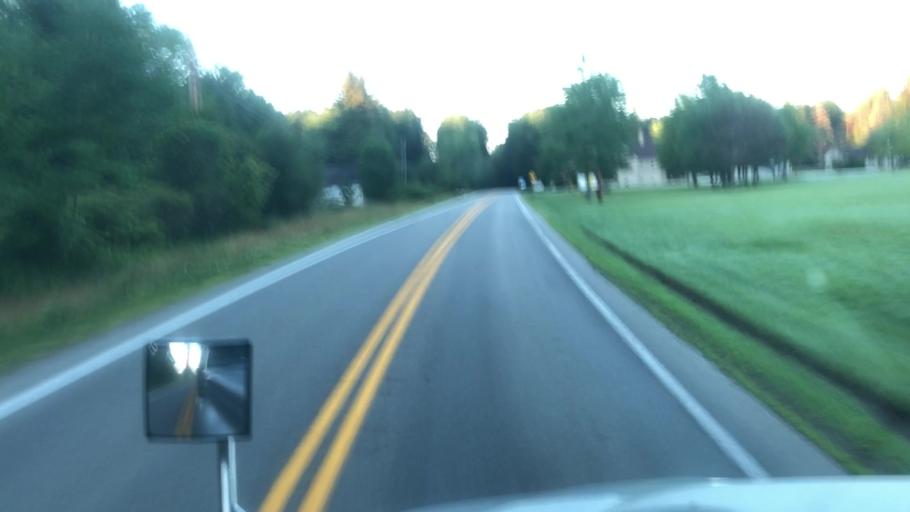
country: US
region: Pennsylvania
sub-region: Crawford County
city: Titusville
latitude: 41.5705
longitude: -79.6101
